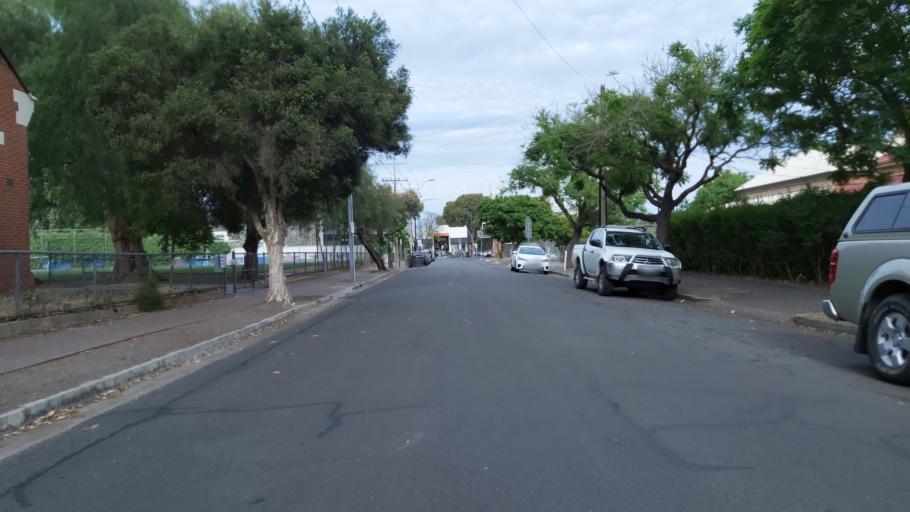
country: AU
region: South Australia
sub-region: Unley
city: Unley
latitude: -34.9536
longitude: 138.6093
